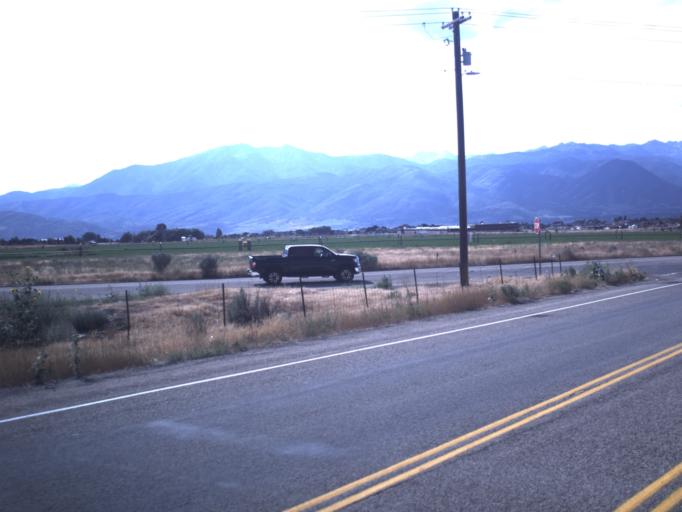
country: US
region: Utah
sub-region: Wasatch County
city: Heber
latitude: 40.4748
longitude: -111.3947
